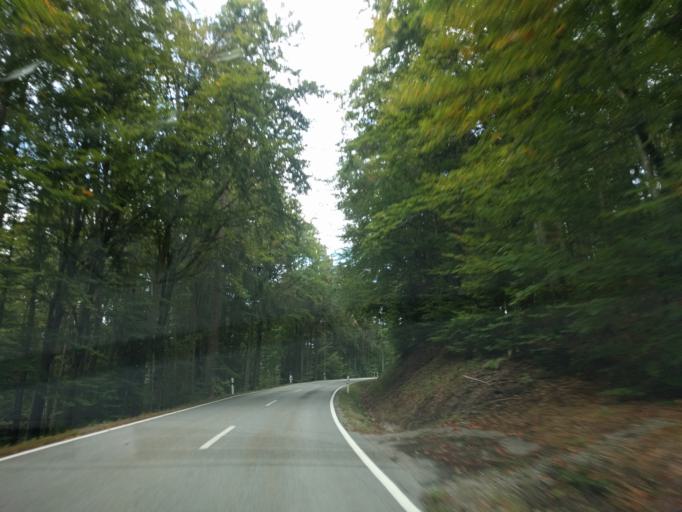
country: DE
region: Bavaria
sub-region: Lower Bavaria
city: Grafling
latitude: 48.8652
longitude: 12.9799
